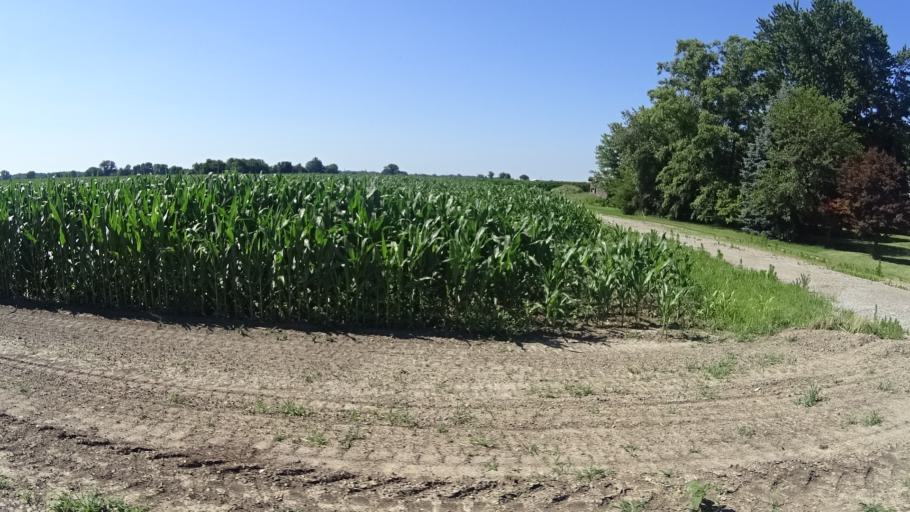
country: US
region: Ohio
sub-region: Erie County
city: Huron
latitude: 41.3893
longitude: -82.6005
